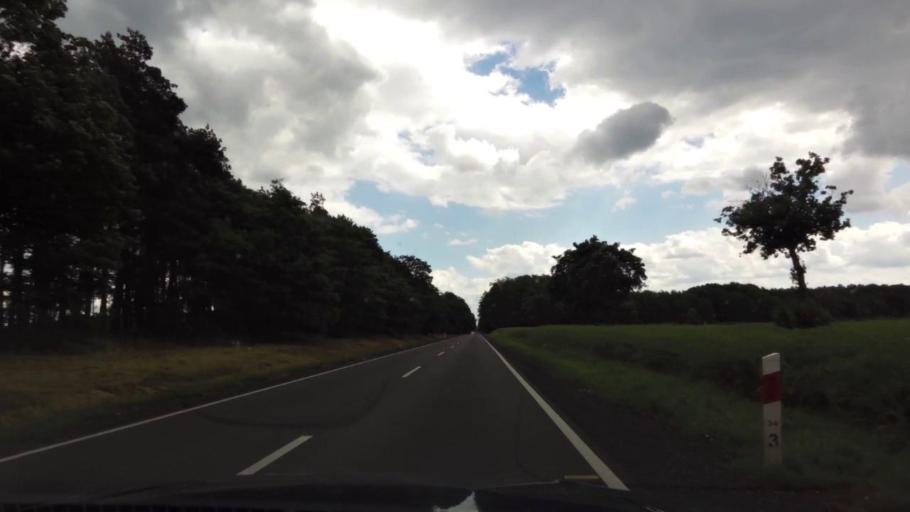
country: PL
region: West Pomeranian Voivodeship
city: Trzcinsko Zdroj
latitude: 52.9744
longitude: 14.7285
